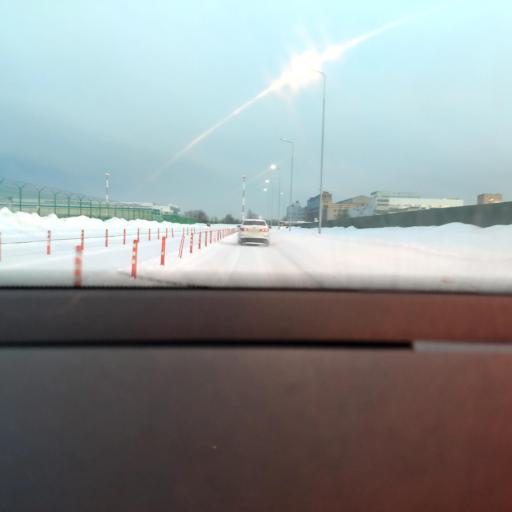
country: RU
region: Moskovskaya
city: Zhukovskiy
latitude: 55.5604
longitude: 38.1179
